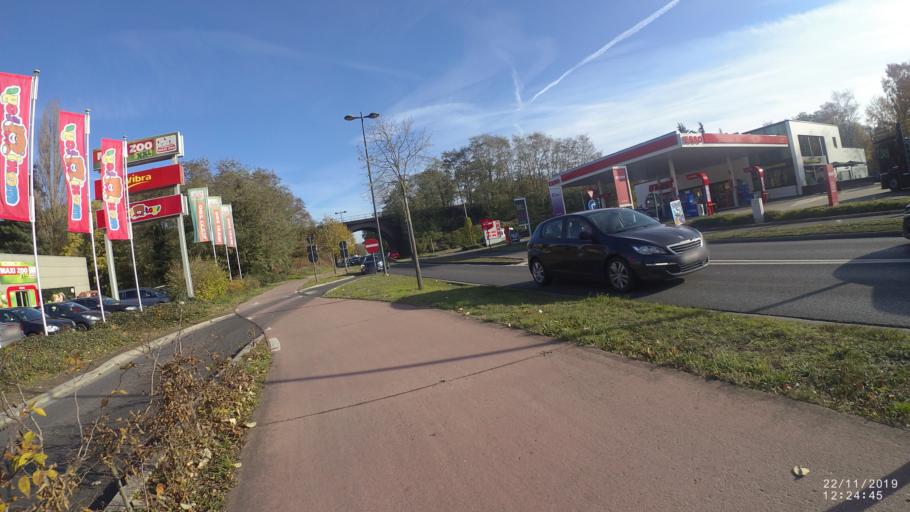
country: BE
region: Flanders
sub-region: Provincie Limburg
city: Genk
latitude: 50.9646
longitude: 5.4744
